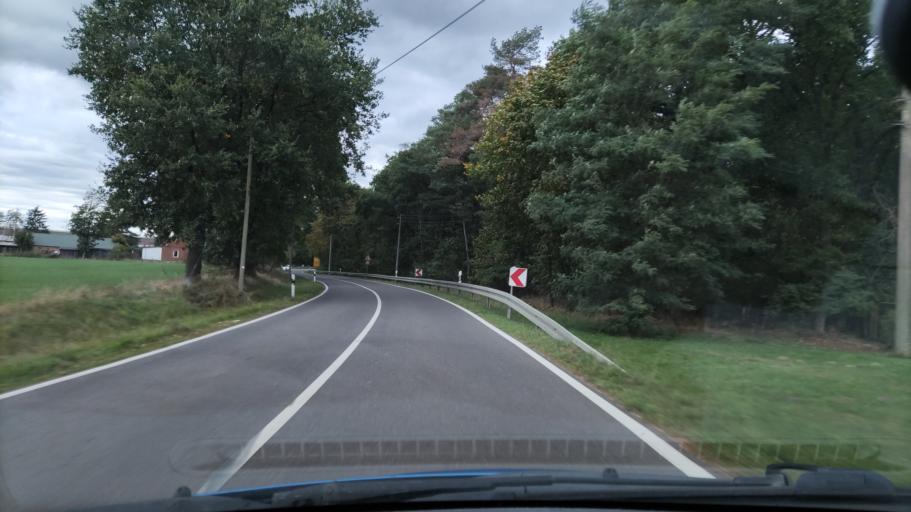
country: DE
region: Mecklenburg-Vorpommern
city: Lubtheen
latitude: 53.3535
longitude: 10.9604
